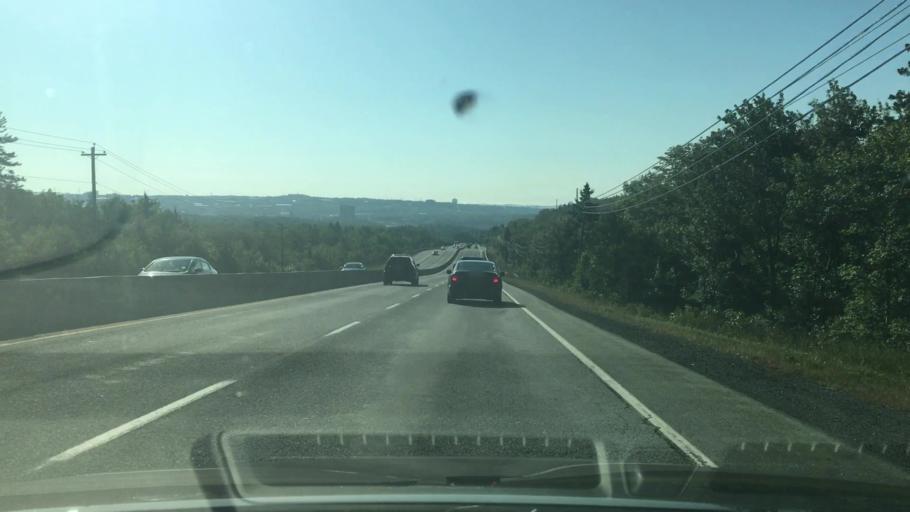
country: CA
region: Nova Scotia
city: Dartmouth
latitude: 44.7157
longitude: -63.6324
